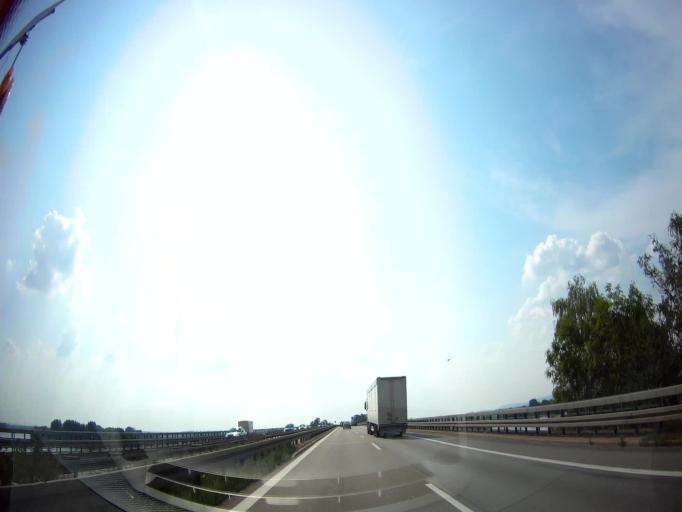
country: DE
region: Bavaria
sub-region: Upper Palatinate
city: Wiesent
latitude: 48.9995
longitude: 12.3469
